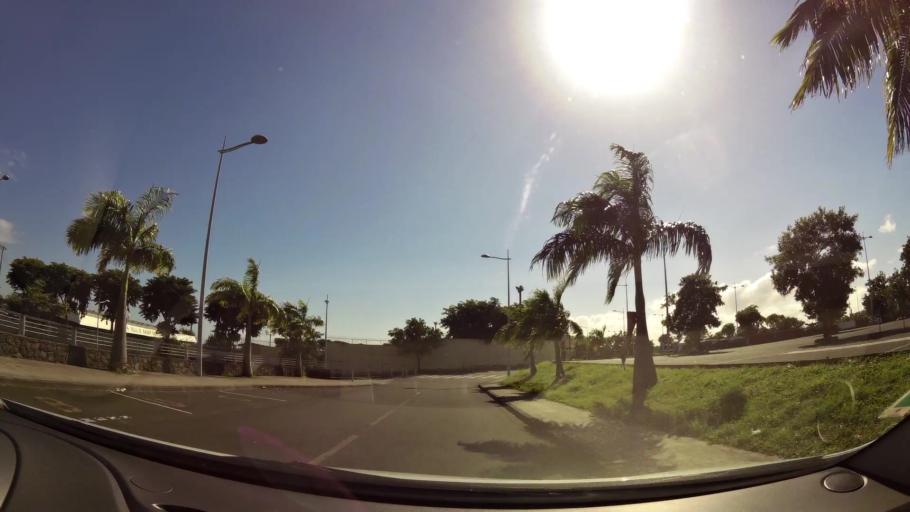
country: RE
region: Reunion
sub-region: Reunion
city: Sainte-Marie
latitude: -20.8962
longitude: 55.5020
